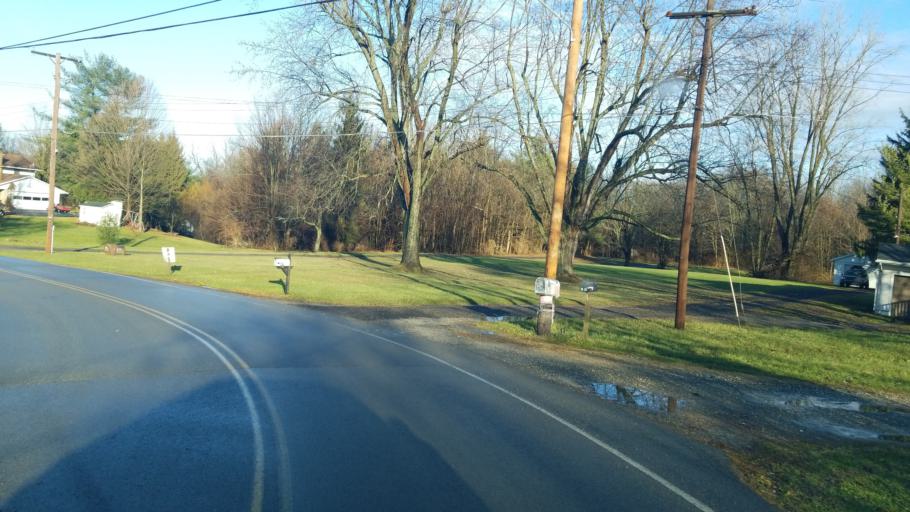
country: US
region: Ohio
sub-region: Richland County
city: Mansfield
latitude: 40.7276
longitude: -82.5002
